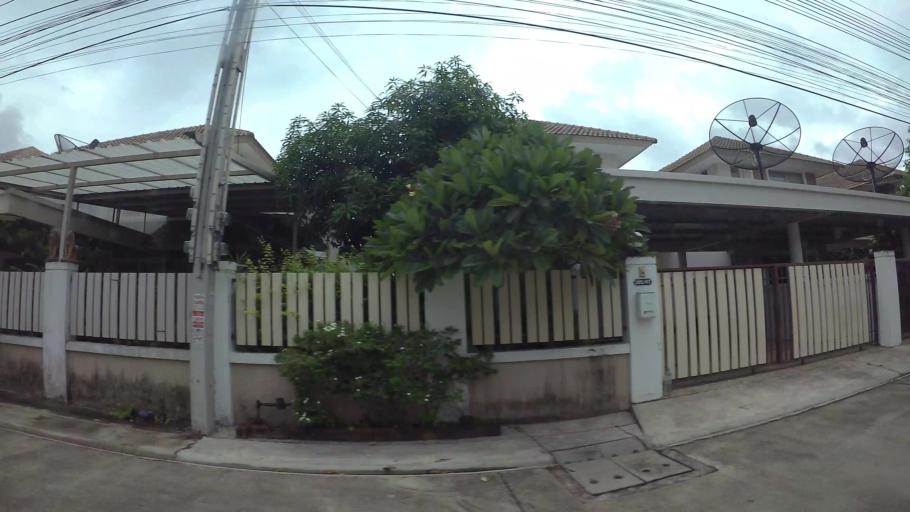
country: TH
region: Chon Buri
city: Si Racha
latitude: 13.2078
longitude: 100.9473
